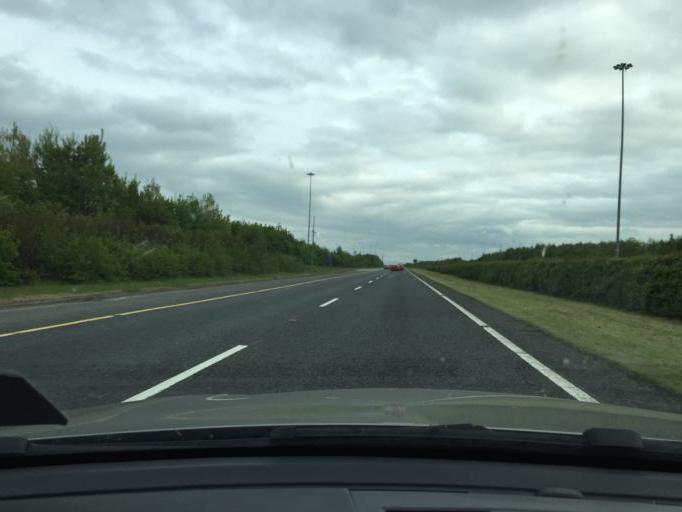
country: IE
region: Leinster
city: Balrothery
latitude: 53.5620
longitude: -6.2141
